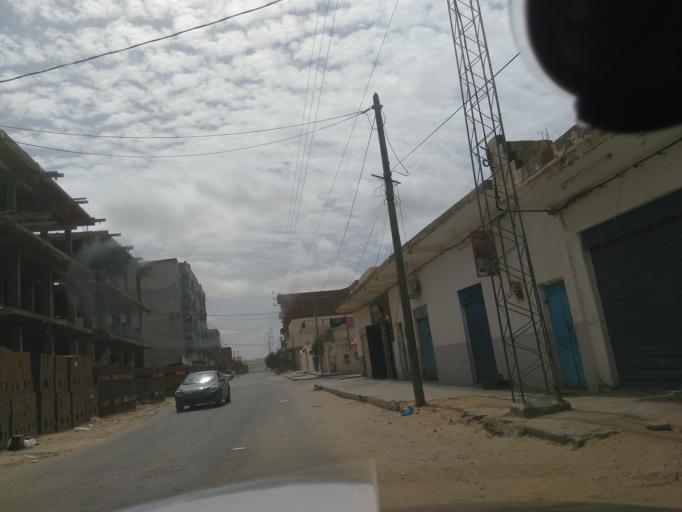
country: TN
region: Tataouine
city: Tataouine
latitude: 32.9523
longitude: 10.4694
